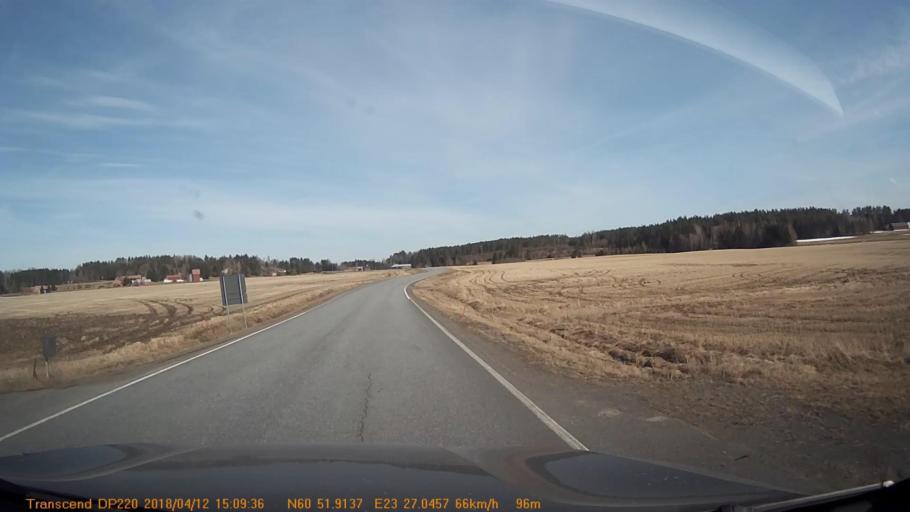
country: FI
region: Haeme
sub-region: Forssa
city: Jokioinen
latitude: 60.8653
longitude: 23.4514
